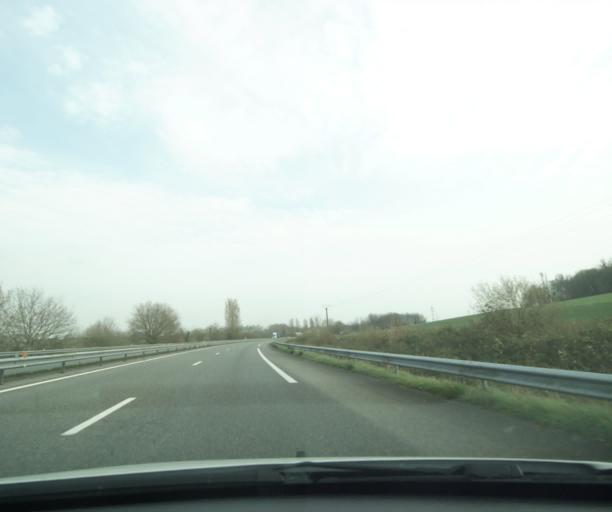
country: FR
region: Aquitaine
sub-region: Departement des Pyrenees-Atlantiques
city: Puyoo
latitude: 43.5079
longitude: -0.8442
